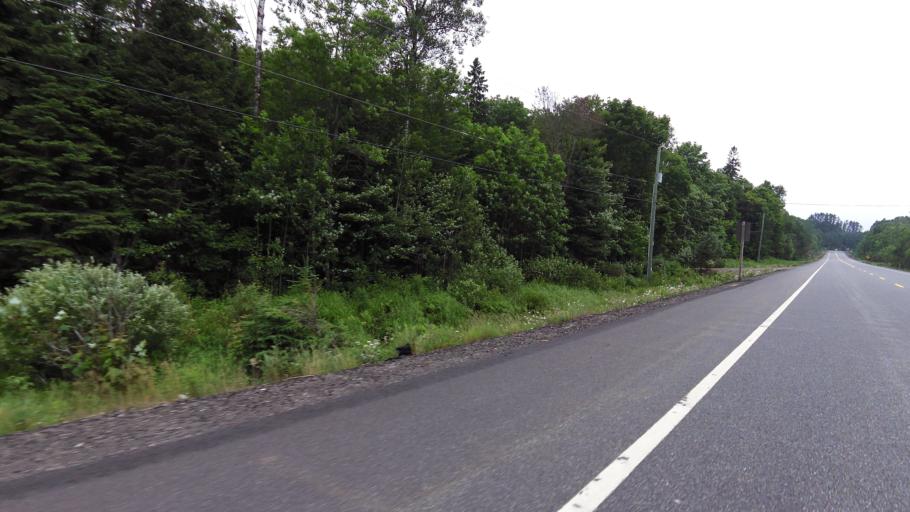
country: CA
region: Ontario
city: Huntsville
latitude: 45.3728
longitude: -78.9271
